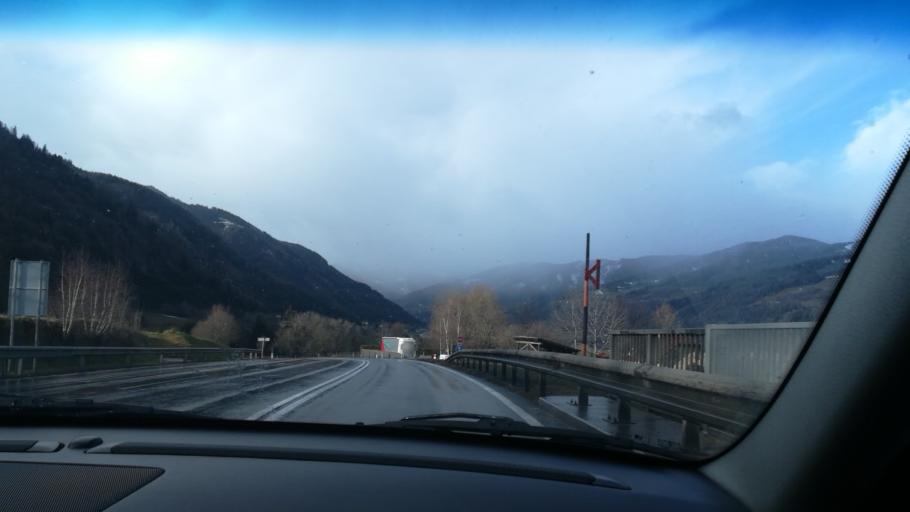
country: AT
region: Styria
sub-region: Politischer Bezirk Murtal
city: Sankt Georgen ob Judenburg
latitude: 47.2013
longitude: 14.5294
